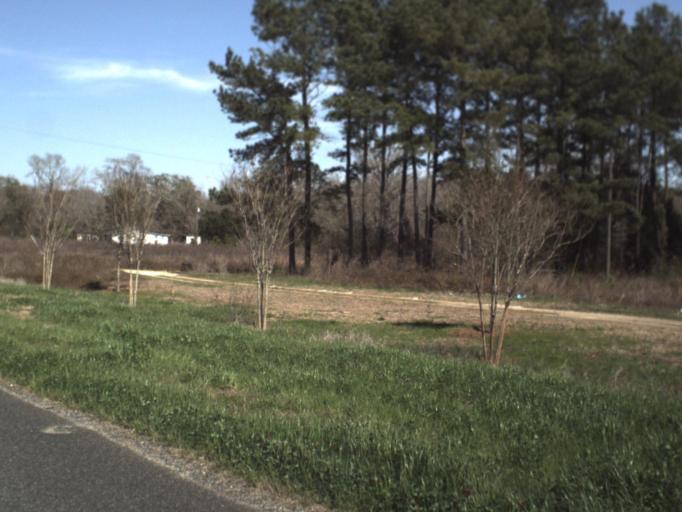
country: US
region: Alabama
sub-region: Houston County
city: Cottonwood
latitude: 30.9963
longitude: -85.4076
